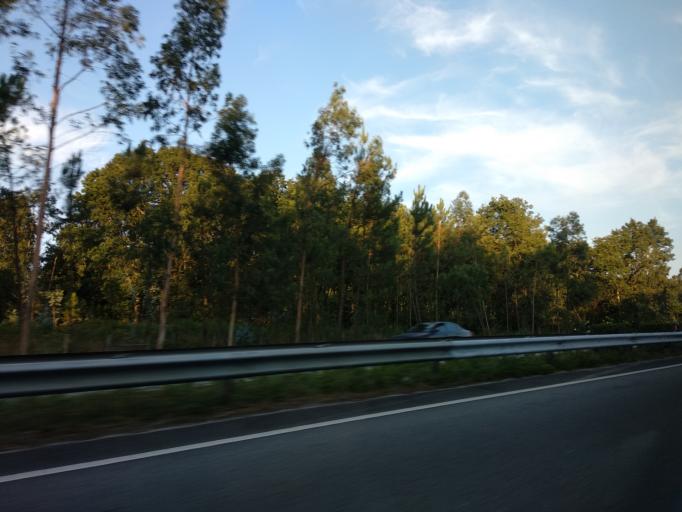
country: PT
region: Braga
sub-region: Vila Verde
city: Prado
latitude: 41.5961
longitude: -8.4423
